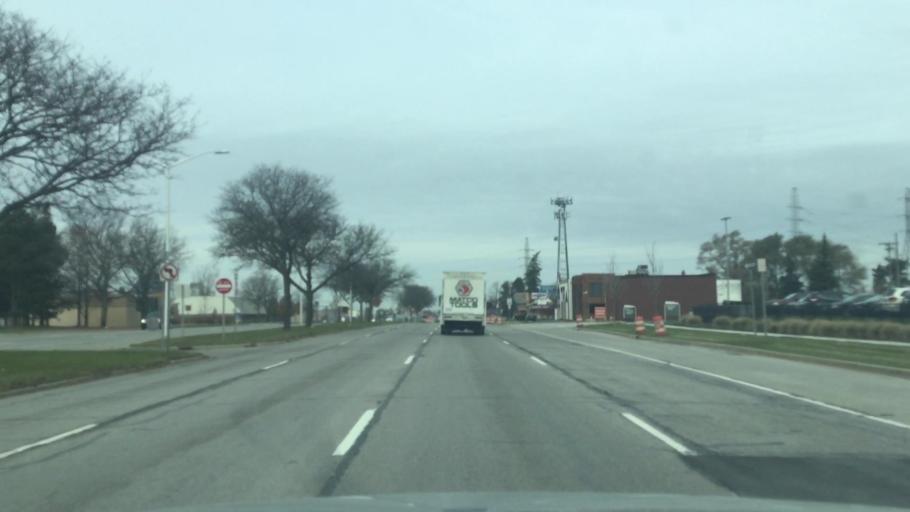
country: US
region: Michigan
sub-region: Oakland County
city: Pontiac
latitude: 42.6164
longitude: -83.2761
